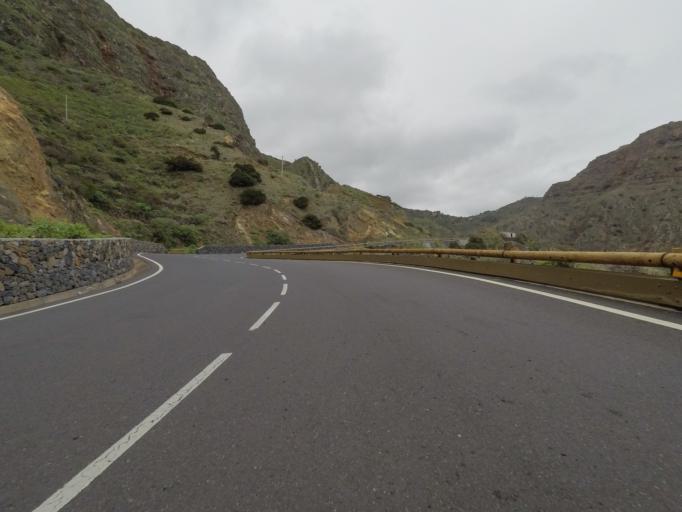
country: ES
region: Canary Islands
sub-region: Provincia de Santa Cruz de Tenerife
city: Agulo
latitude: 28.1910
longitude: -17.2036
